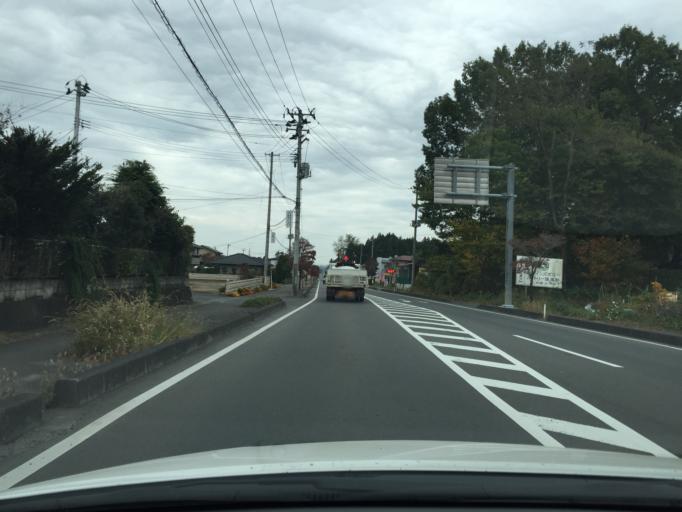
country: JP
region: Tochigi
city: Kuroiso
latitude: 37.1025
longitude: 140.2297
